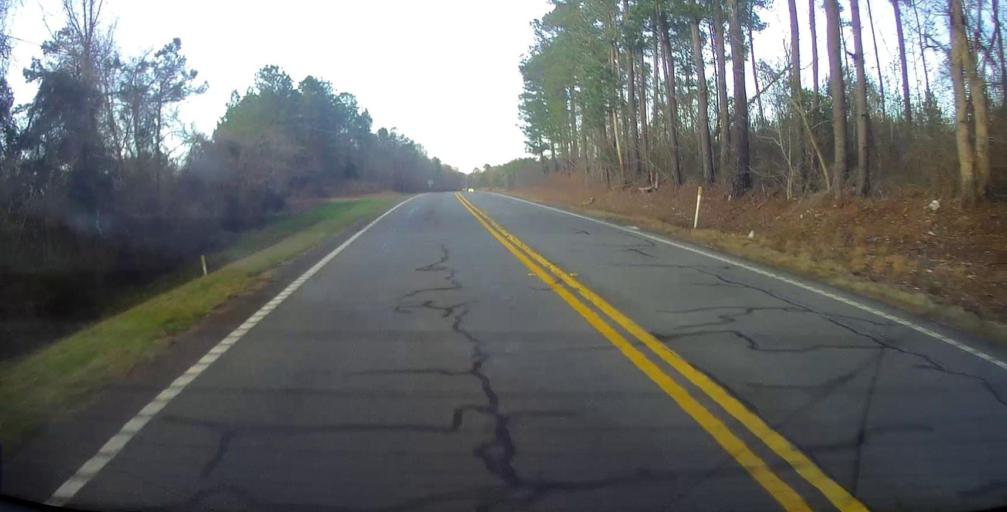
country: US
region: Georgia
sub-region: Talbot County
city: Sardis
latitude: 32.7731
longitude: -84.5579
